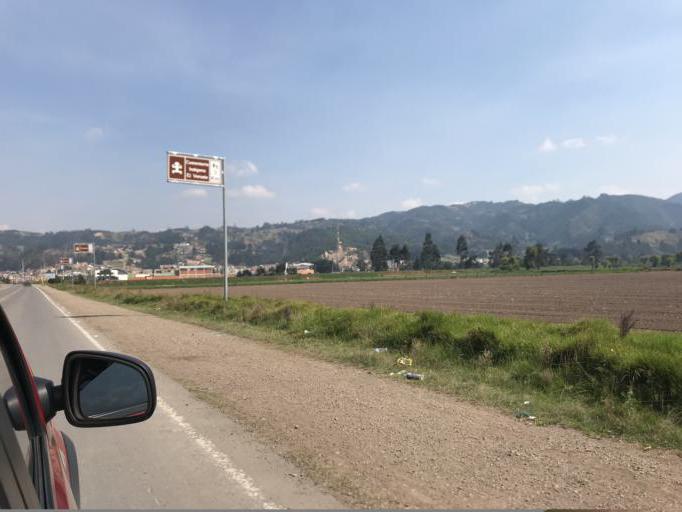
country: CO
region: Boyaca
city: Samaca
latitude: 5.5004
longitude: -73.4926
